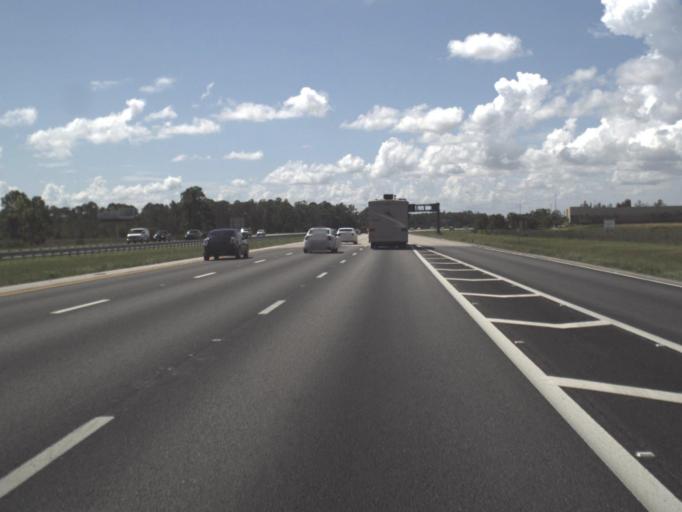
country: US
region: Florida
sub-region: Lee County
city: Tice
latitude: 26.6523
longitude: -81.7996
